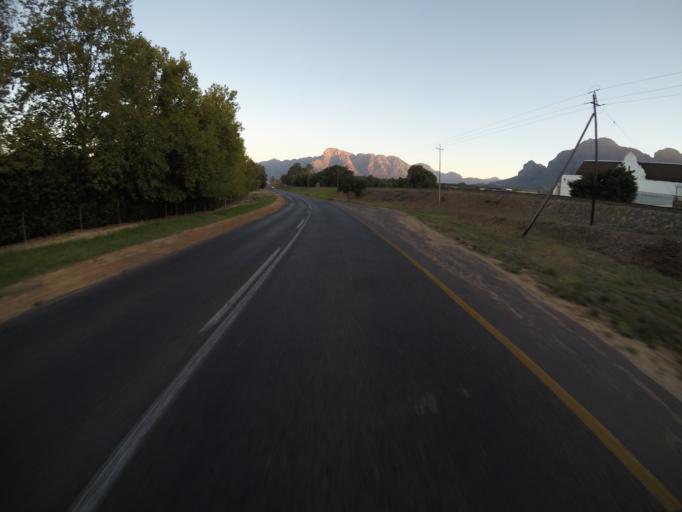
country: ZA
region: Western Cape
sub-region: Cape Winelands District Municipality
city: Paarl
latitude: -33.8371
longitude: 18.9541
